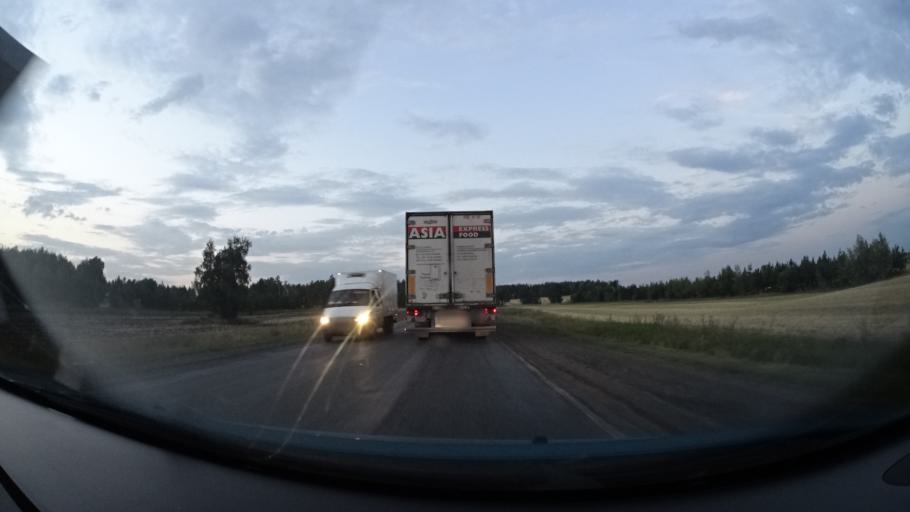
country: RU
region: Tatarstan
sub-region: Bavlinskiy Rayon
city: Bavly
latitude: 54.2841
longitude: 52.9937
